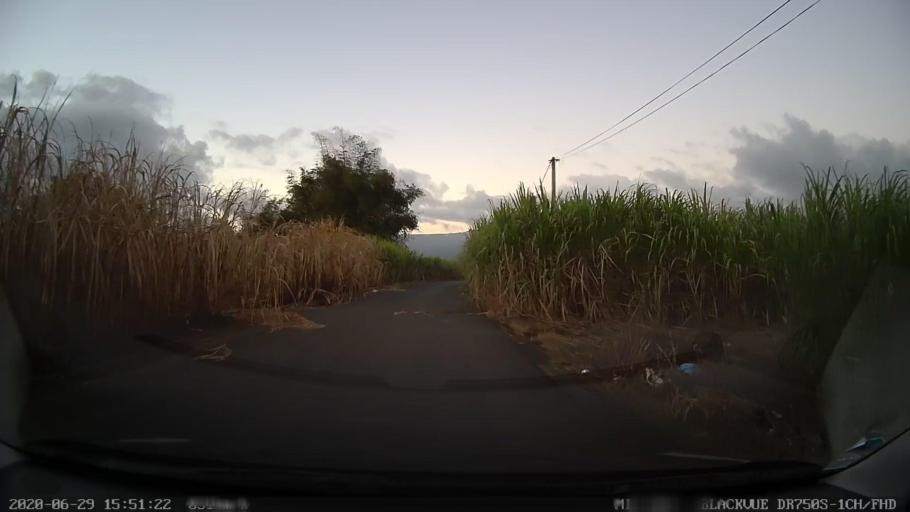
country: RE
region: Reunion
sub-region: Reunion
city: Bras-Panon
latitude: -20.9937
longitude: 55.6936
